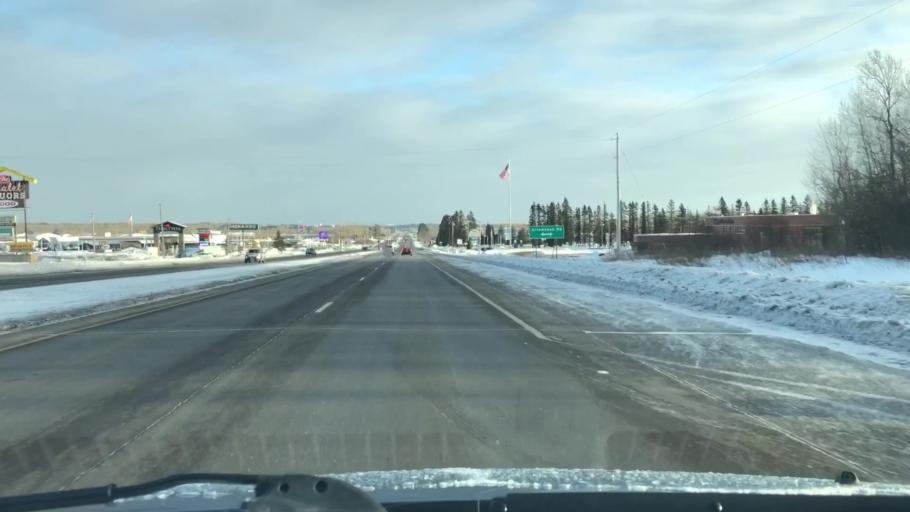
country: US
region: Minnesota
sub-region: Saint Louis County
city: Hermantown
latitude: 46.8243
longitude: -92.1904
